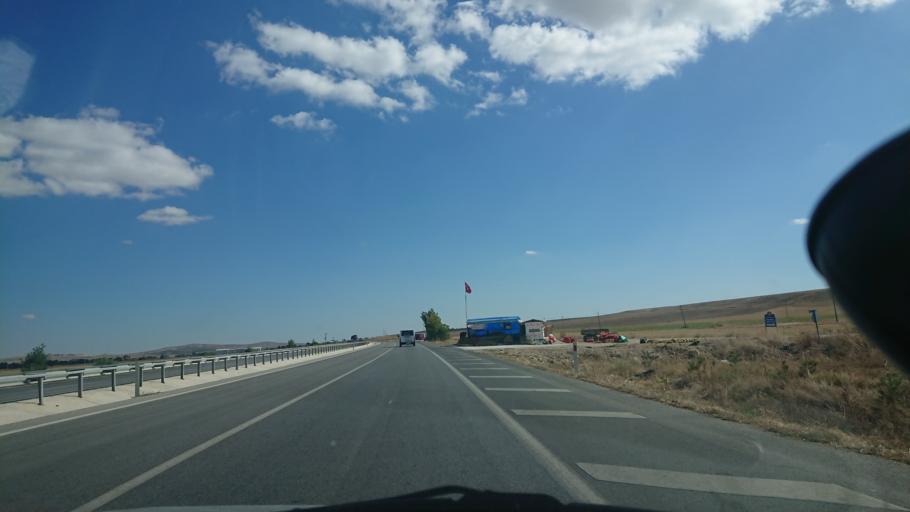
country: TR
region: Eskisehir
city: Mahmudiye
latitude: 39.5332
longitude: 30.9467
